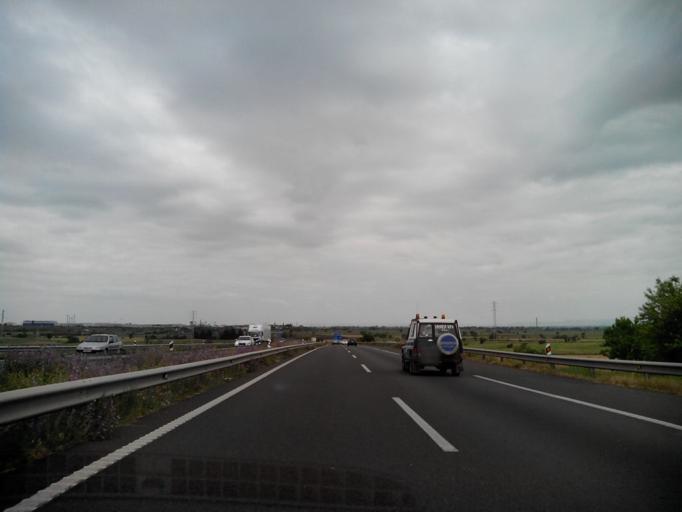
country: ES
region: Catalonia
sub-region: Provincia de Lleida
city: Tarrega
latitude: 41.6571
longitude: 1.1171
